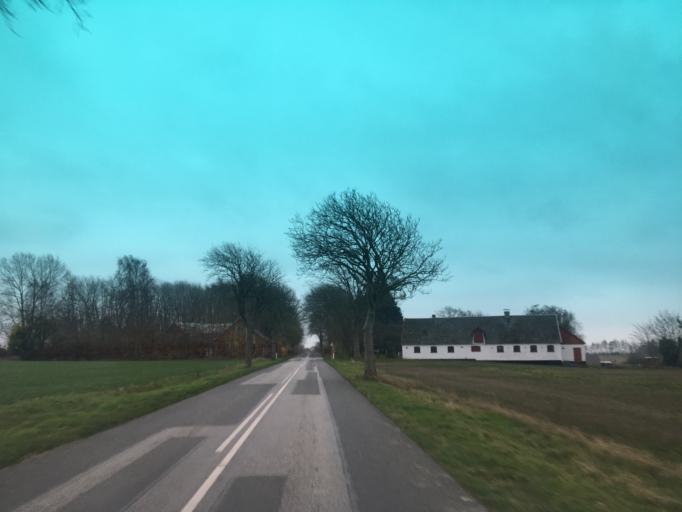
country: DK
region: Zealand
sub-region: Slagelse Kommune
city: Skaelskor
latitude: 55.2518
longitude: 11.4197
